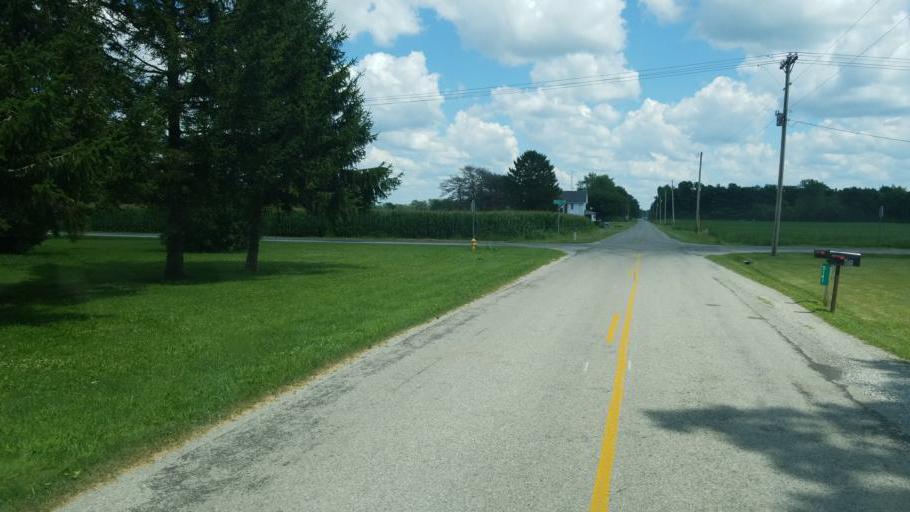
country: US
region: Ohio
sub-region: Marion County
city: Marion
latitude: 40.6382
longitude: -82.9915
